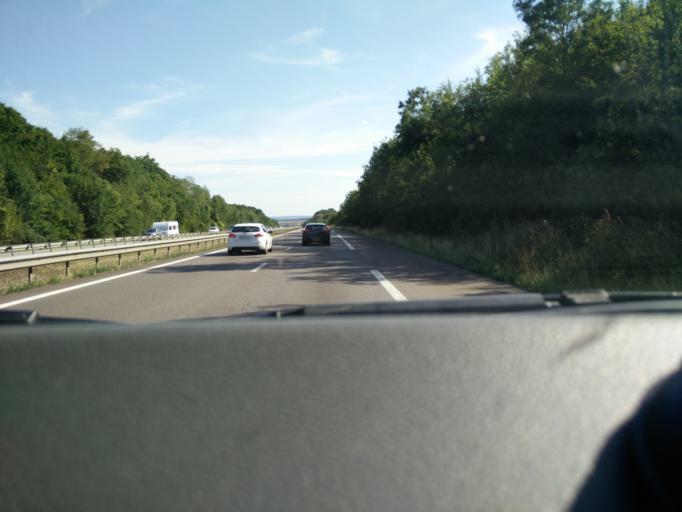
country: FR
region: Lorraine
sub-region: Departement de Meurthe-et-Moselle
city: Pont-a-Mousson
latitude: 48.9665
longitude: 6.1056
